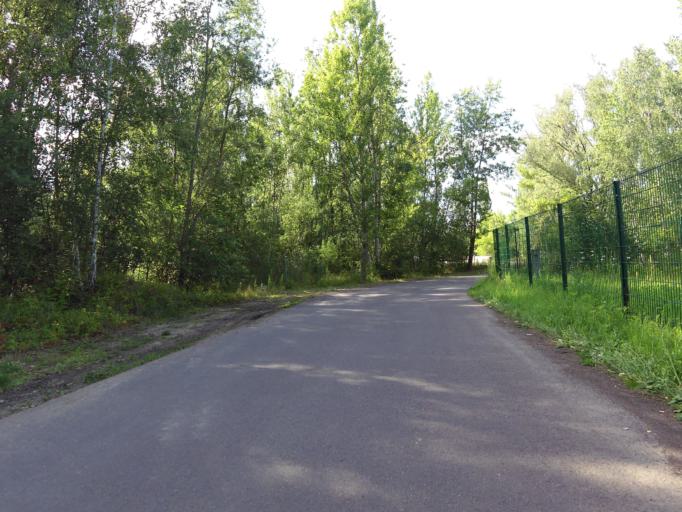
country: DE
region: Saxony
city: Leipzig
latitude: 51.3289
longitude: 12.3038
